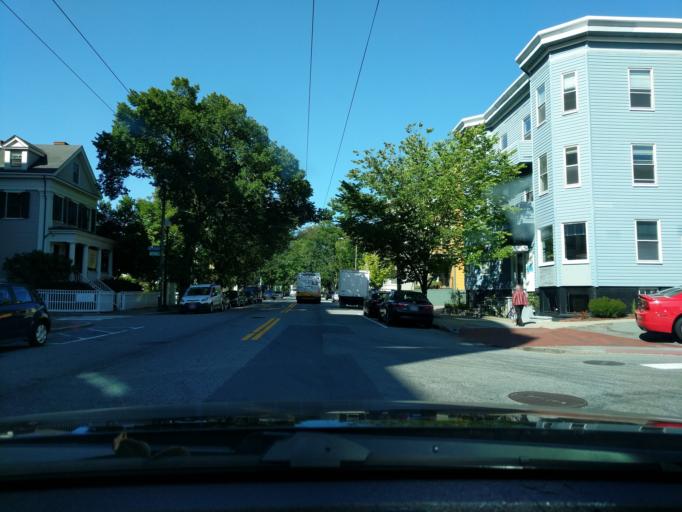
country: US
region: Massachusetts
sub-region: Middlesex County
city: Cambridge
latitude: 42.3735
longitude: -71.1232
